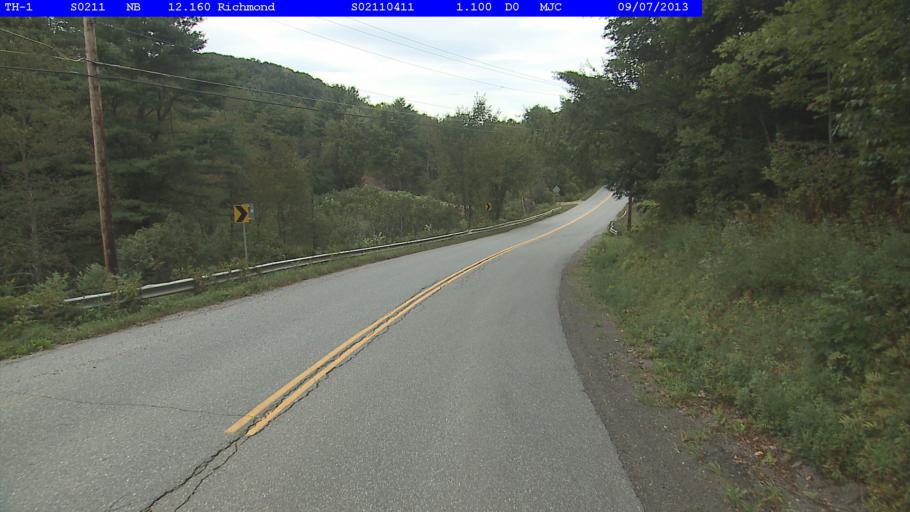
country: US
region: Vermont
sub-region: Chittenden County
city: Williston
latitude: 44.3674
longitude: -72.9995
